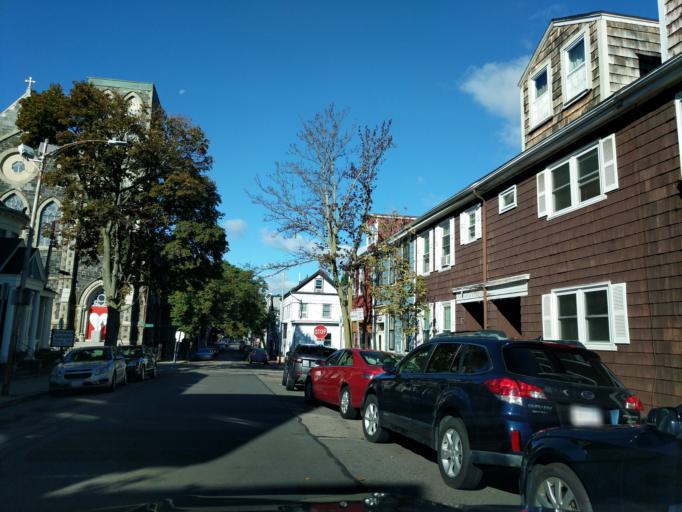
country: US
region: Massachusetts
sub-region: Middlesex County
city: Cambridge
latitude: 42.3709
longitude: -71.0845
